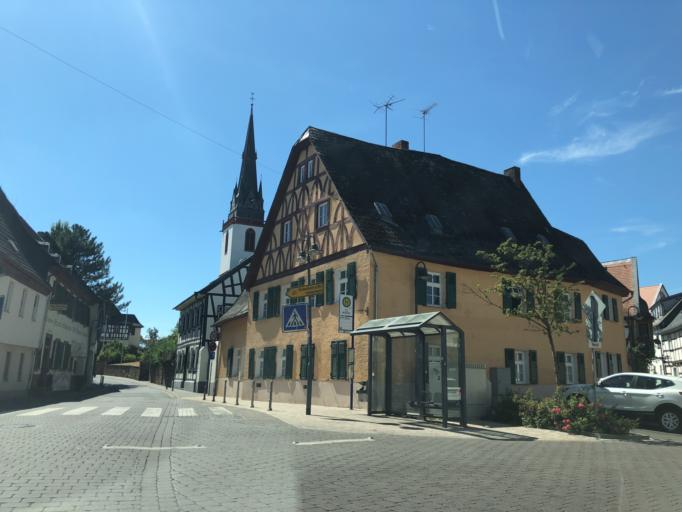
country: DE
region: Hesse
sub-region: Regierungsbezirk Darmstadt
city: Kiedrich
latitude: 50.0202
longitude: 8.0949
